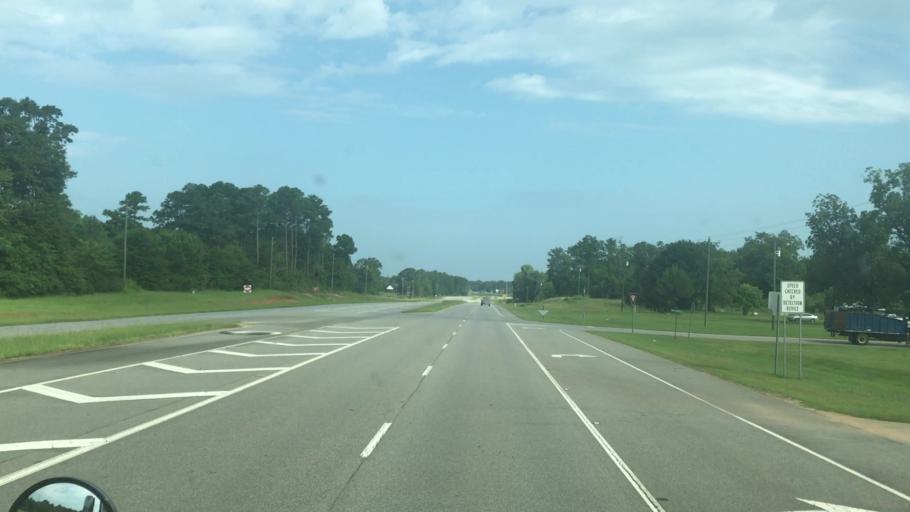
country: US
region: Georgia
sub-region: Early County
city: Blakely
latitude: 31.3502
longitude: -84.9160
